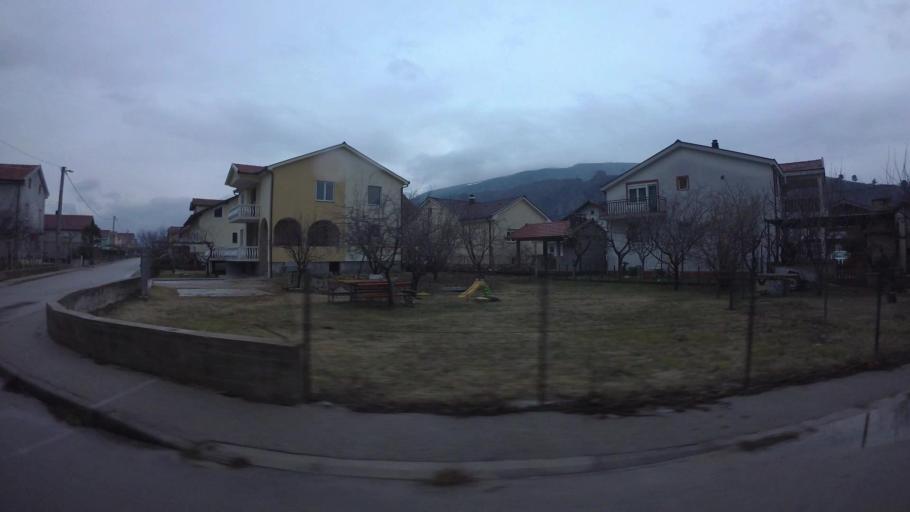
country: BA
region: Federation of Bosnia and Herzegovina
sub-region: Hercegovacko-Bosanski Kanton
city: Mostar
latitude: 43.3673
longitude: 17.8181
